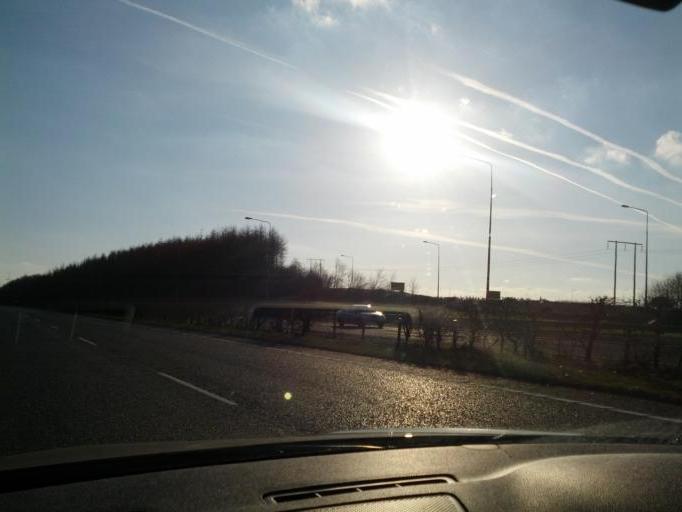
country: IE
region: Leinster
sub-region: Laois
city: Portlaoise
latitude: 53.0529
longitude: -7.2363
